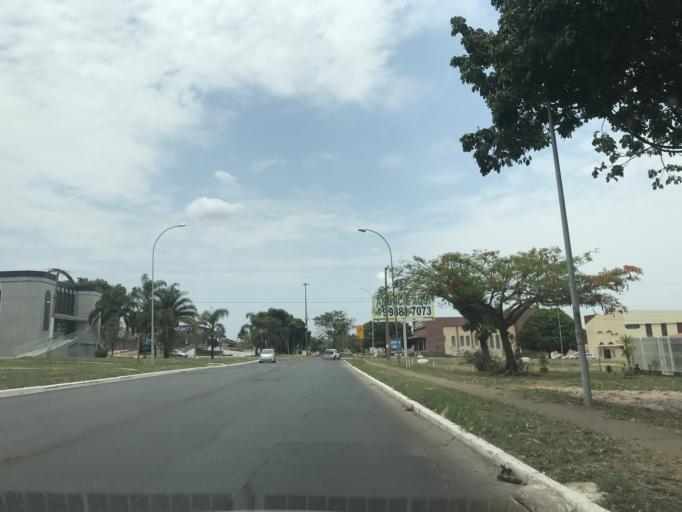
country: BR
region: Federal District
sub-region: Brasilia
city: Brasilia
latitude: -15.6509
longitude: -47.8039
